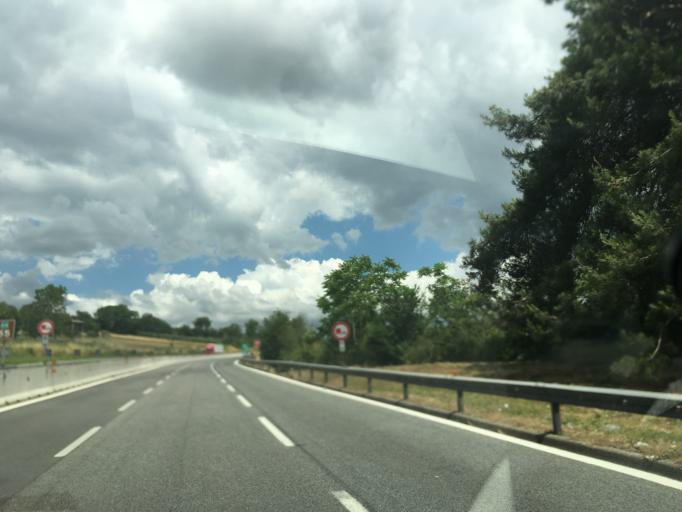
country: IT
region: Campania
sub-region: Provincia di Avellino
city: Campanarello
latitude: 41.0726
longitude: 14.9521
